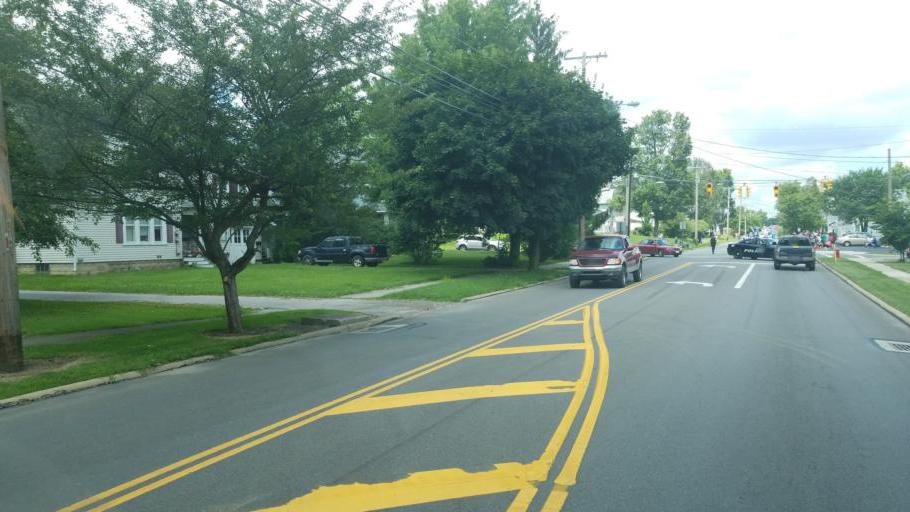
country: US
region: Ohio
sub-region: Richland County
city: Shelby
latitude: 40.8759
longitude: -82.6625
